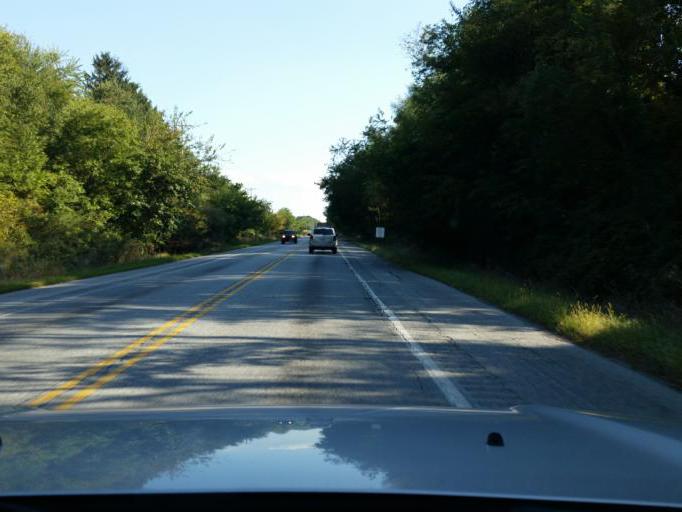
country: US
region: Pennsylvania
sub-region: Chester County
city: Atglen
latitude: 39.9264
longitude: -75.9476
